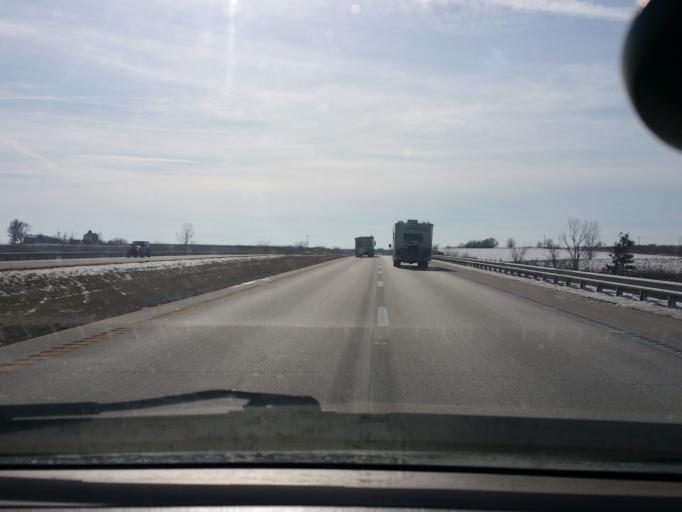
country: US
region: Missouri
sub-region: Clinton County
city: Lathrop
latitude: 39.5766
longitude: -94.2606
